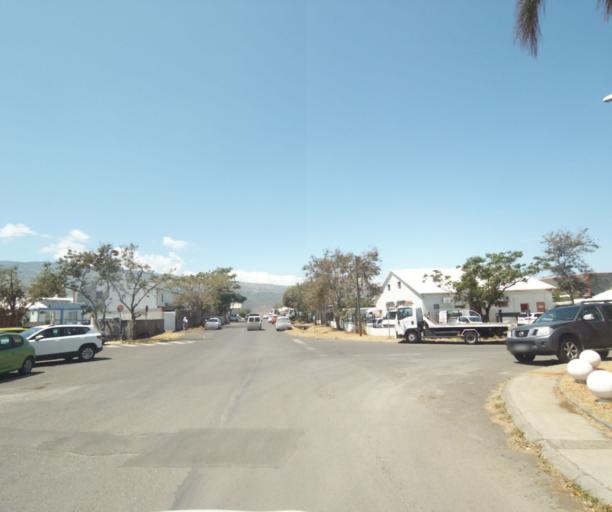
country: RE
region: Reunion
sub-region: Reunion
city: Le Port
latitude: -20.9624
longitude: 55.2978
